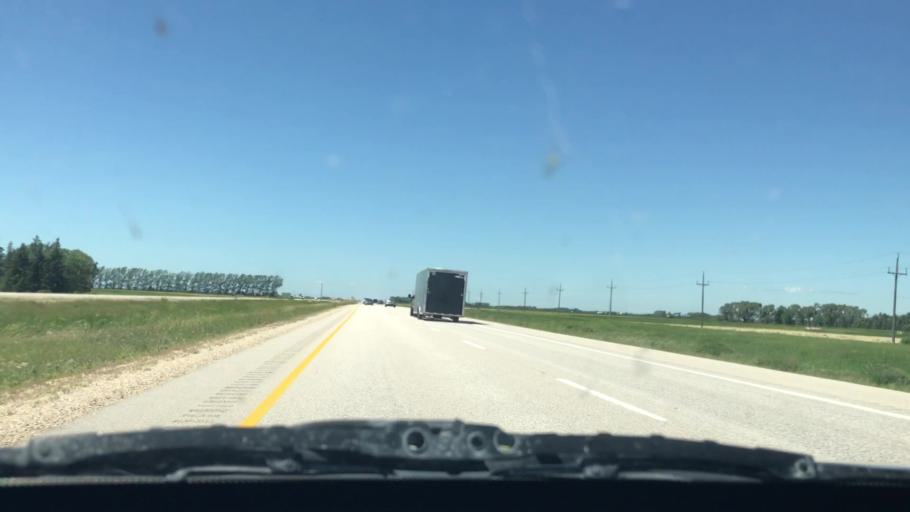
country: CA
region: Manitoba
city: Steinbach
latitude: 49.7312
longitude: -96.7212
